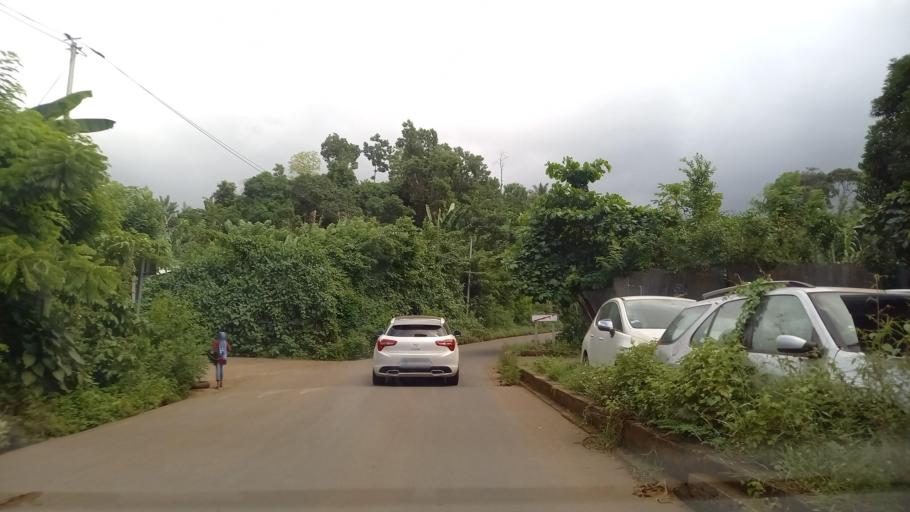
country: YT
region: Mamoudzou
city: Mamoudzou
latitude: -12.7862
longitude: 45.1745
